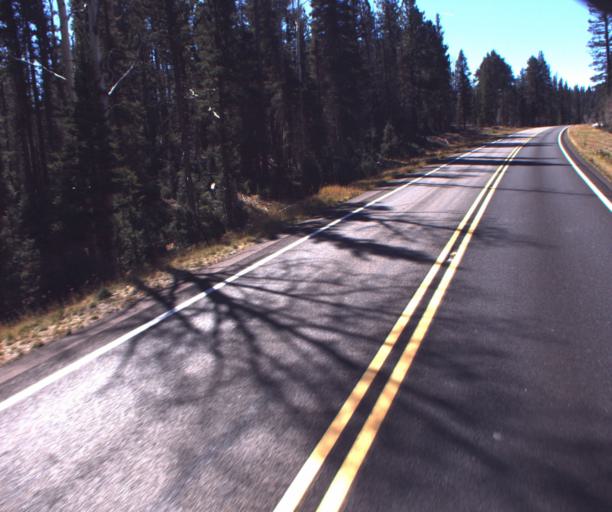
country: US
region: Arizona
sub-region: Coconino County
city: Grand Canyon
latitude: 36.4556
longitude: -112.1310
